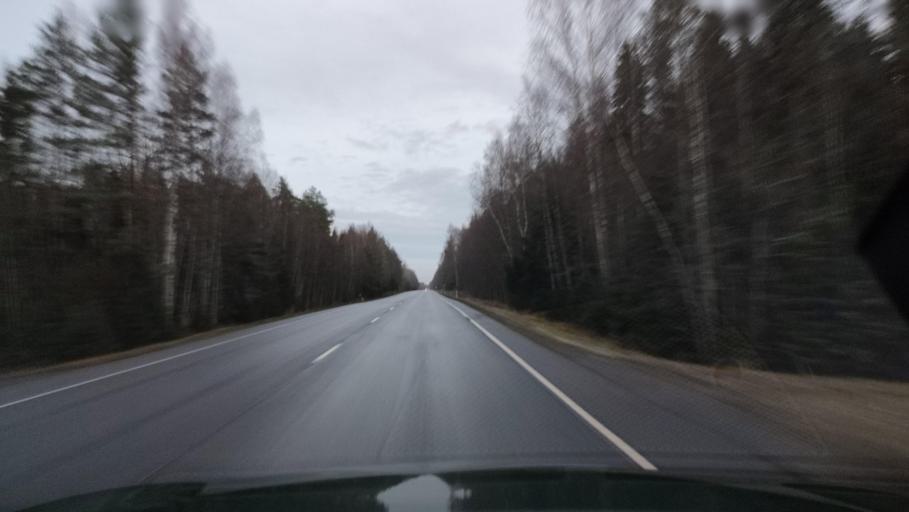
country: FI
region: Ostrobothnia
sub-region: Vaasa
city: Ristinummi
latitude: 63.0041
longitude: 21.7635
